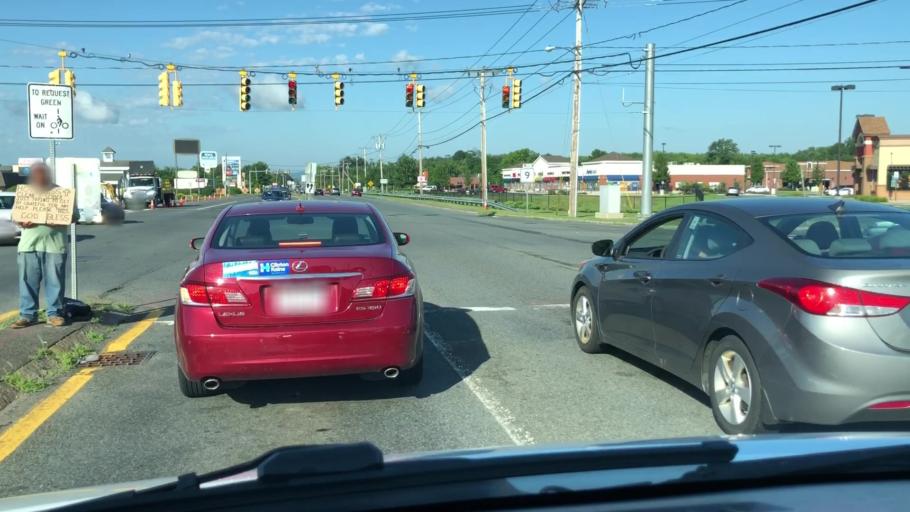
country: US
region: Massachusetts
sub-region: Hampshire County
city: Amherst Center
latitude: 42.3581
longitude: -72.5504
